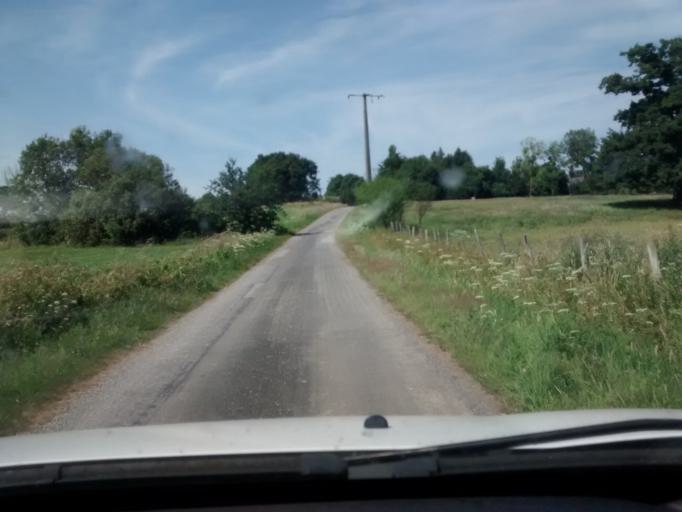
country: FR
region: Brittany
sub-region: Departement d'Ille-et-Vilaine
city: Acigne
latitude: 48.1070
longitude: -1.5598
